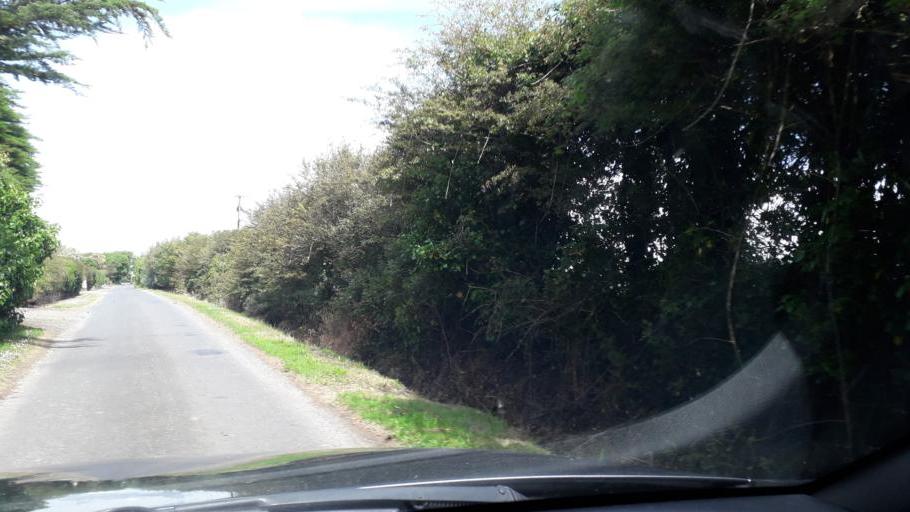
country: IE
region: Leinster
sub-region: Loch Garman
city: Loch Garman
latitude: 52.1908
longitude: -6.5451
